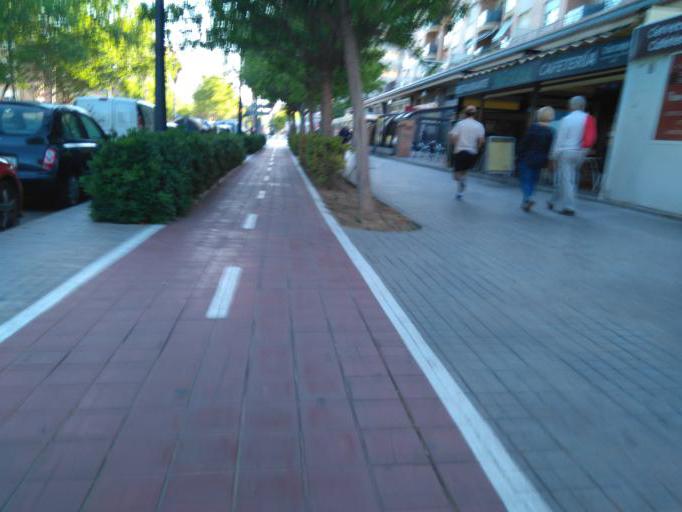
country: ES
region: Valencia
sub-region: Provincia de Valencia
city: Tavernes Blanques
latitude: 39.4935
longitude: -0.3594
